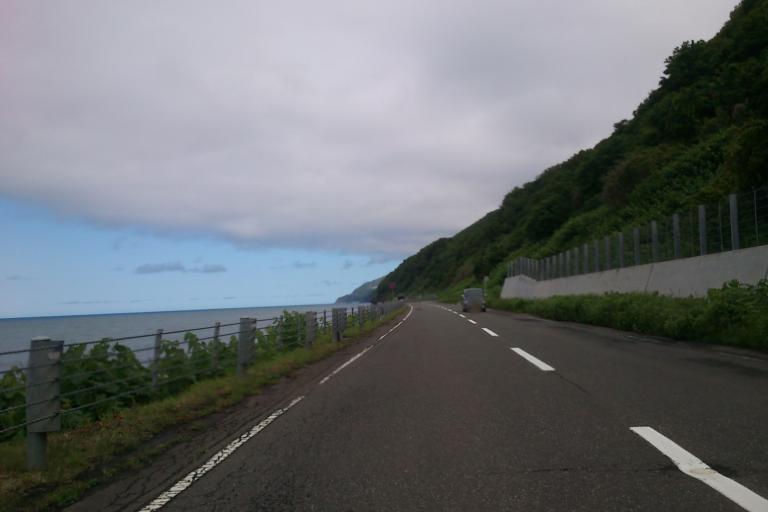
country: JP
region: Hokkaido
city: Ishikari
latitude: 43.4306
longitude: 141.4210
